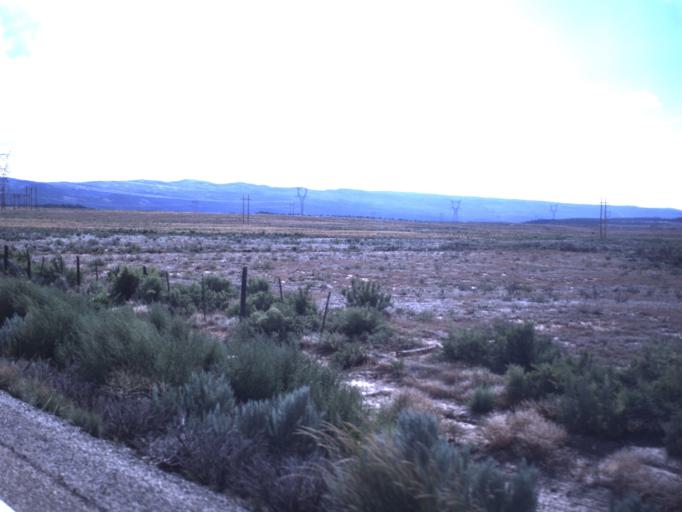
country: US
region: Utah
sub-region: Duchesne County
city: Duchesne
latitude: 40.2239
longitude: -110.7229
